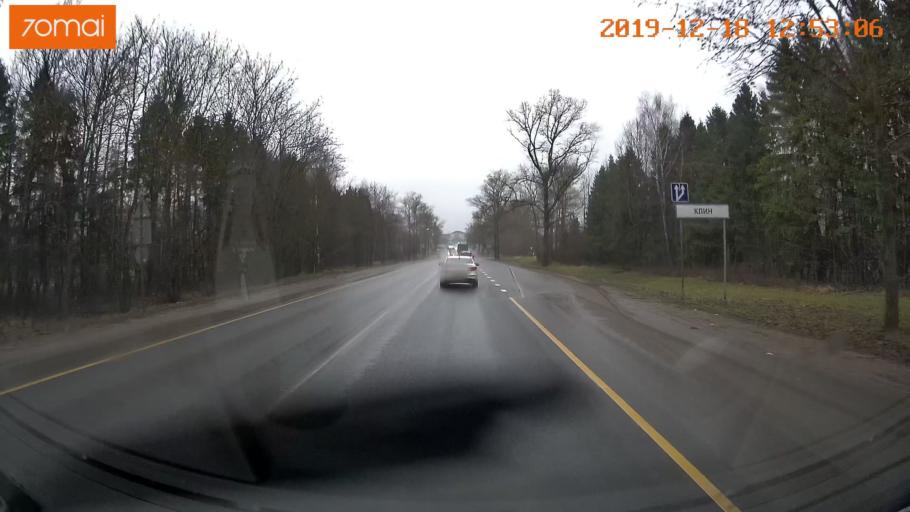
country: RU
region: Moskovskaya
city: Klin
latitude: 56.3162
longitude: 36.6918
